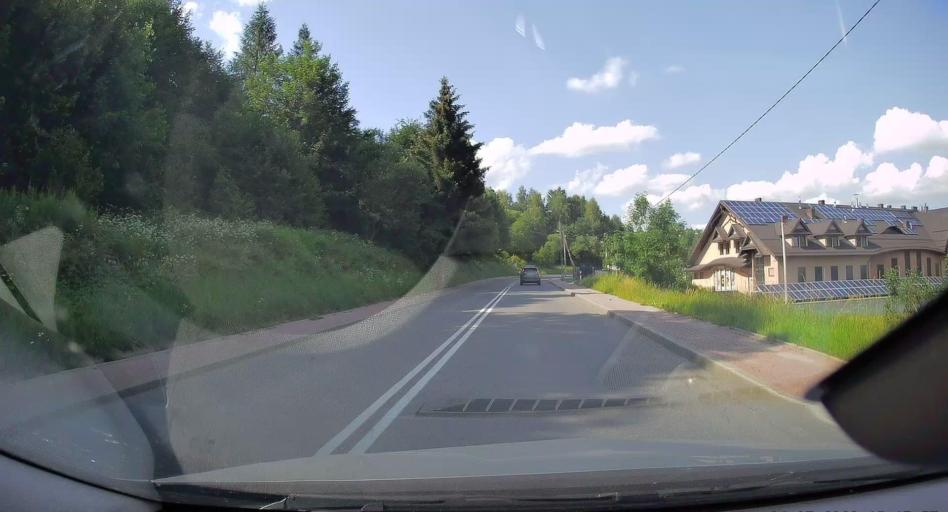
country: PL
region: Lesser Poland Voivodeship
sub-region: Powiat nowosadecki
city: Krynica-Zdroj
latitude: 49.3872
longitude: 20.9508
